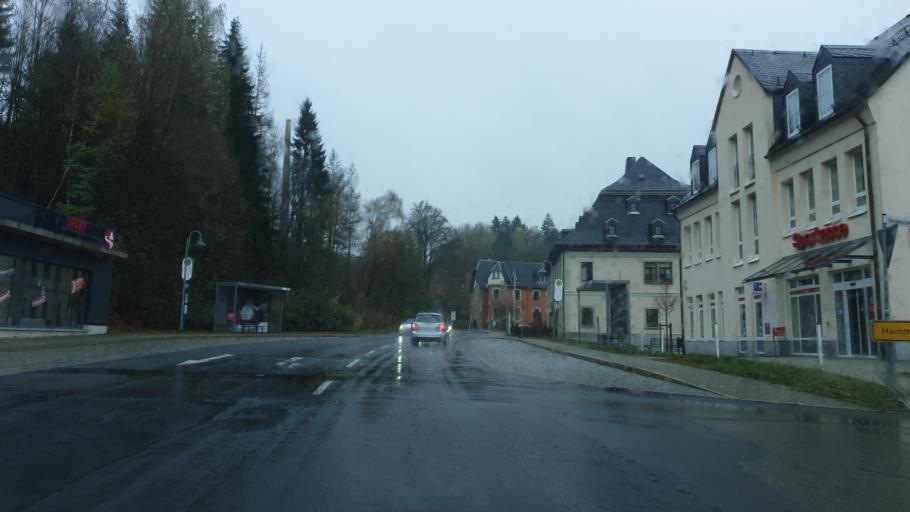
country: DE
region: Saxony
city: Tannenbergsthal
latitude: 50.4356
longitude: 12.4613
